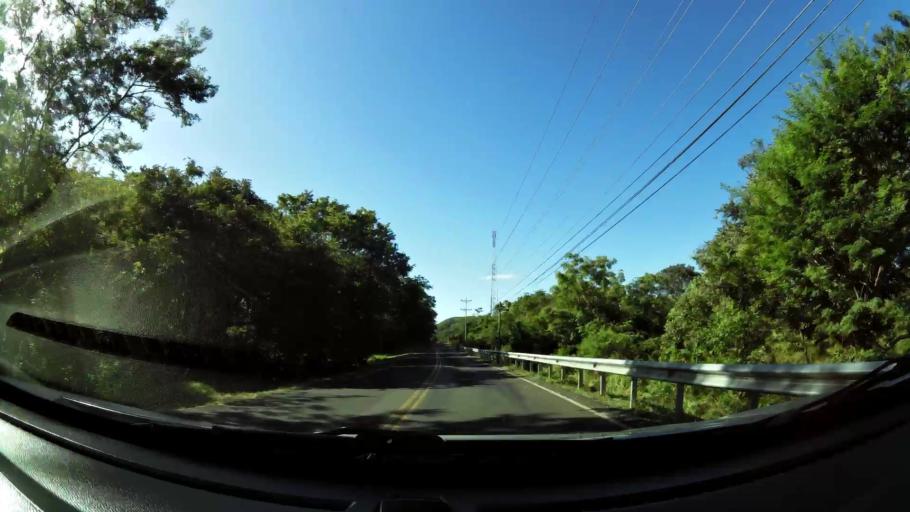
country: CR
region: Guanacaste
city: Belen
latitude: 10.3675
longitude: -85.6446
